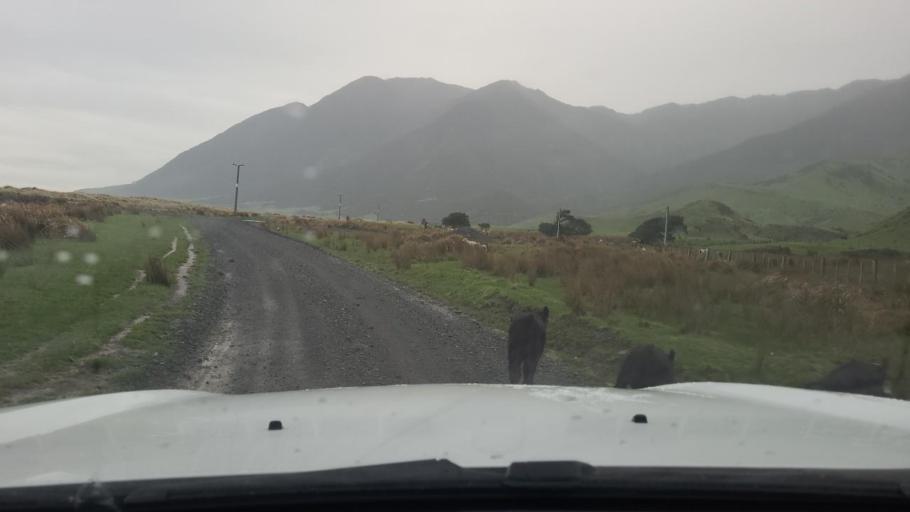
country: NZ
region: Wellington
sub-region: South Wairarapa District
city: Waipawa
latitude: -41.5666
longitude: 175.3841
